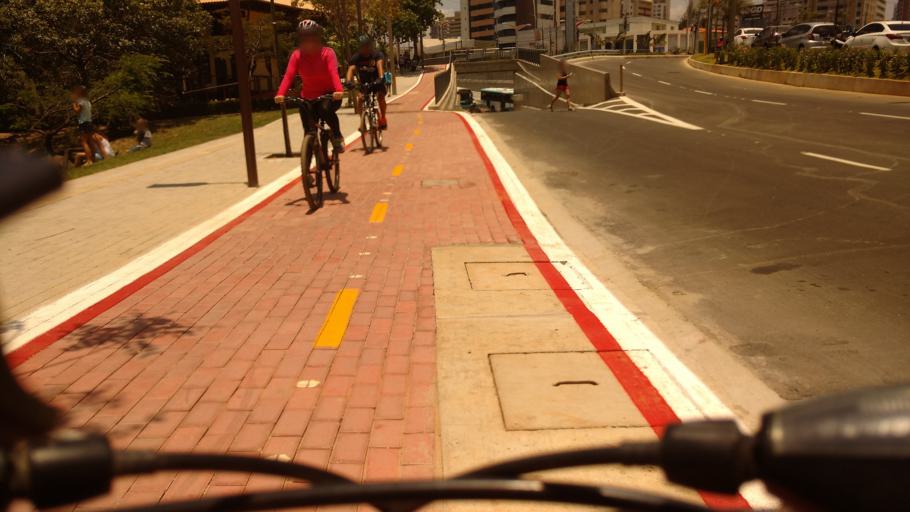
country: BR
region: Ceara
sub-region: Fortaleza
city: Fortaleza
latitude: -3.7439
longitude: -38.4872
